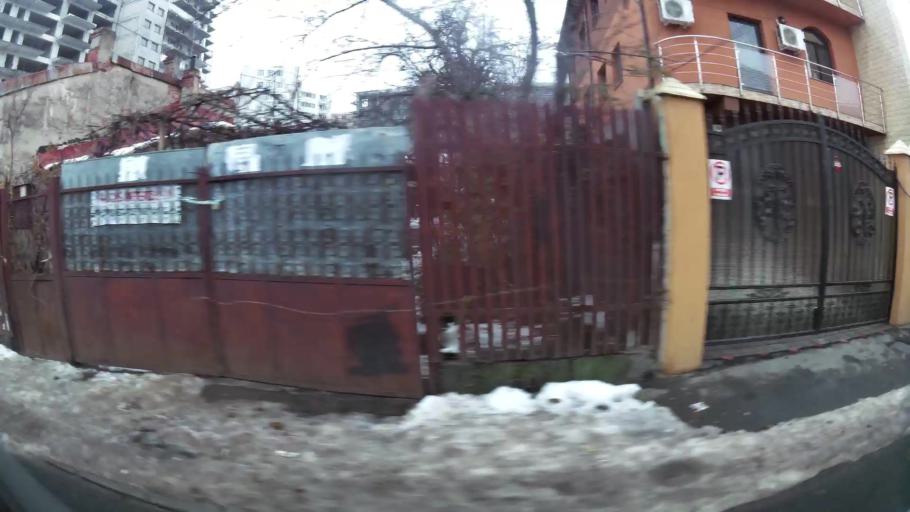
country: RO
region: Bucuresti
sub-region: Municipiul Bucuresti
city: Bucharest
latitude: 44.4138
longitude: 26.1259
